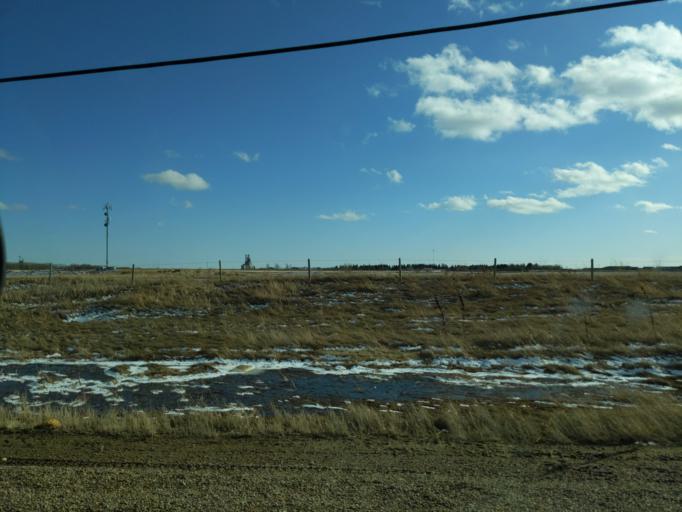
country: CA
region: Saskatchewan
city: Lloydminster
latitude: 53.2752
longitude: -109.9750
